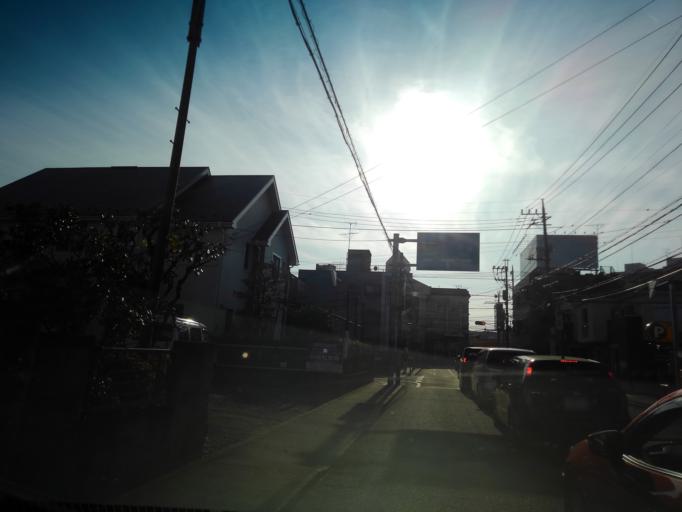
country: JP
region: Saitama
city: Tokorozawa
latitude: 35.8042
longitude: 139.4437
